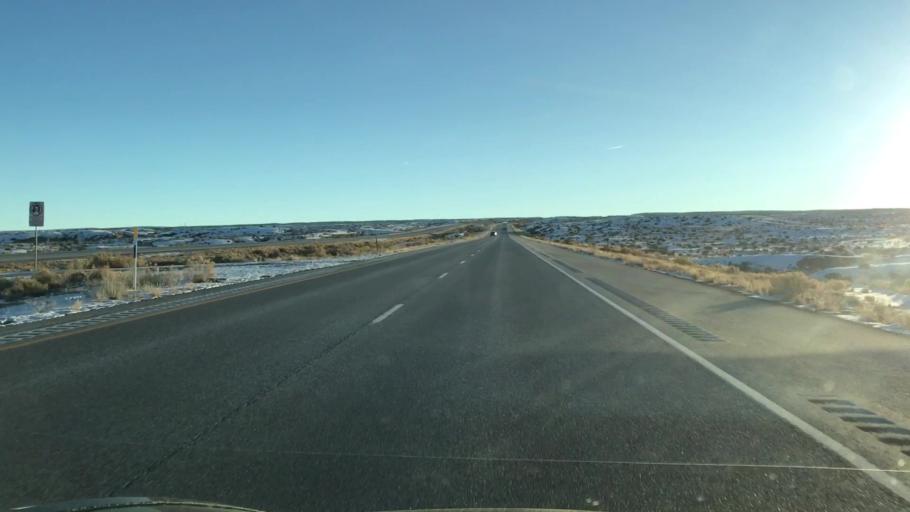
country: US
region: Utah
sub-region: Emery County
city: Ferron
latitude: 38.8467
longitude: -111.0020
